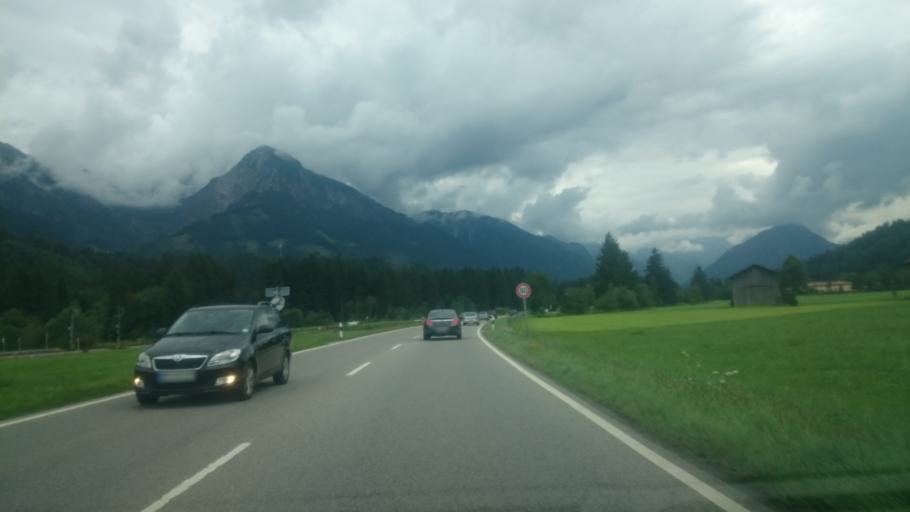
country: DE
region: Bavaria
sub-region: Swabia
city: Obermaiselstein
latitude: 47.4551
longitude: 10.2707
